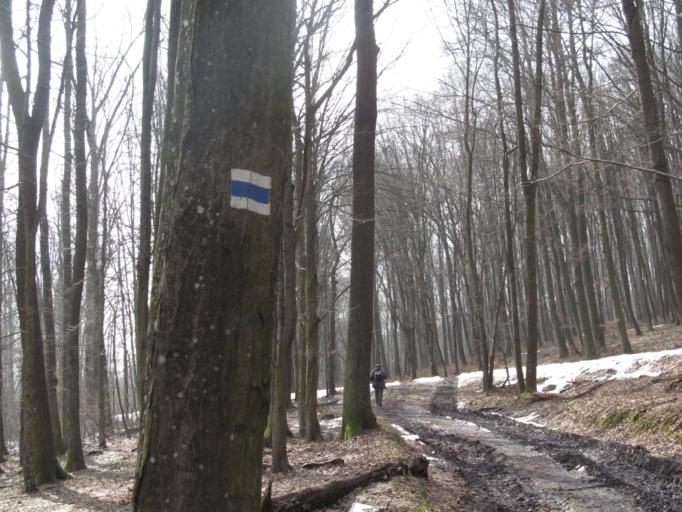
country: HU
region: Veszprem
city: Herend
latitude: 47.2283
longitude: 17.6774
